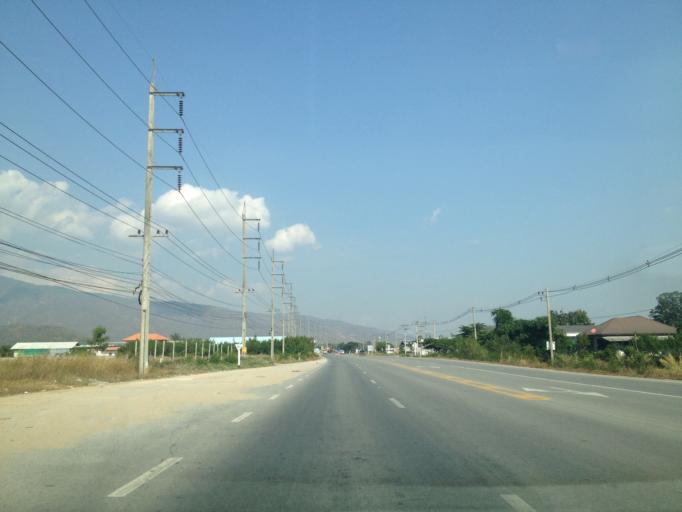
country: TH
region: Chiang Mai
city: Hot
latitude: 18.2854
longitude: 98.6396
